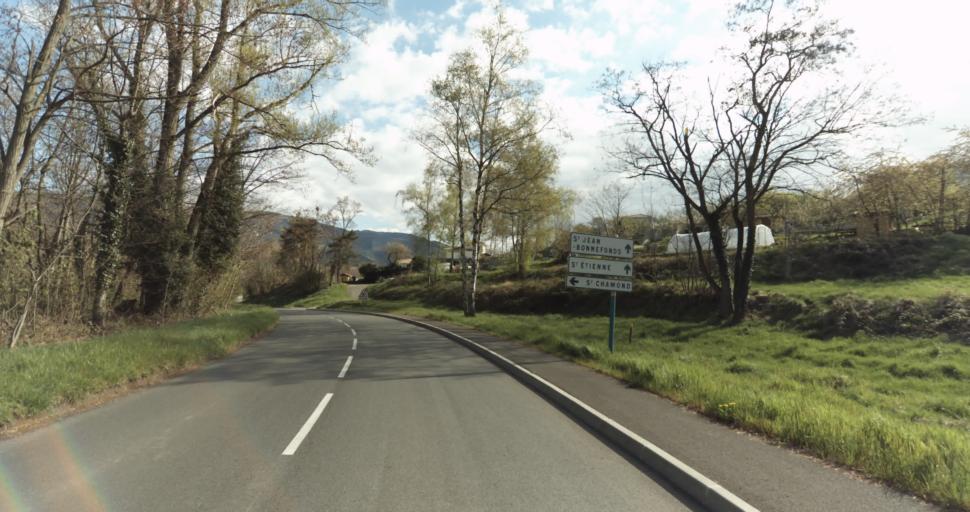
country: FR
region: Rhone-Alpes
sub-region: Departement de la Loire
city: Saint-Jean-Bonnefonds
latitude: 45.4567
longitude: 4.4517
